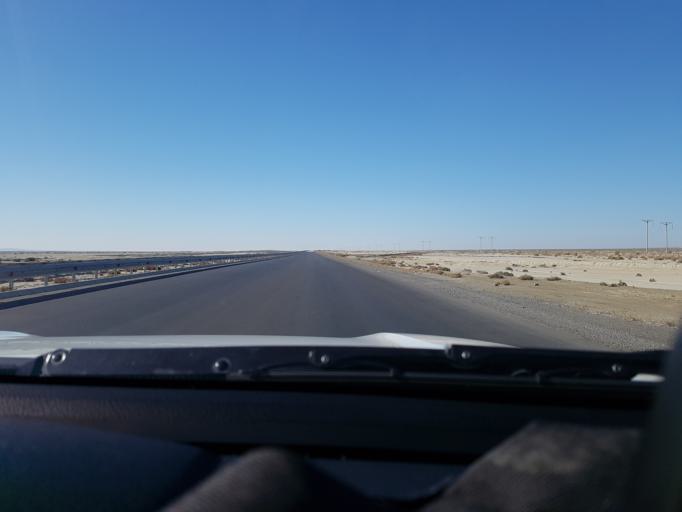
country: TM
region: Balkan
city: Gazanjyk
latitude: 39.2570
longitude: 55.1080
